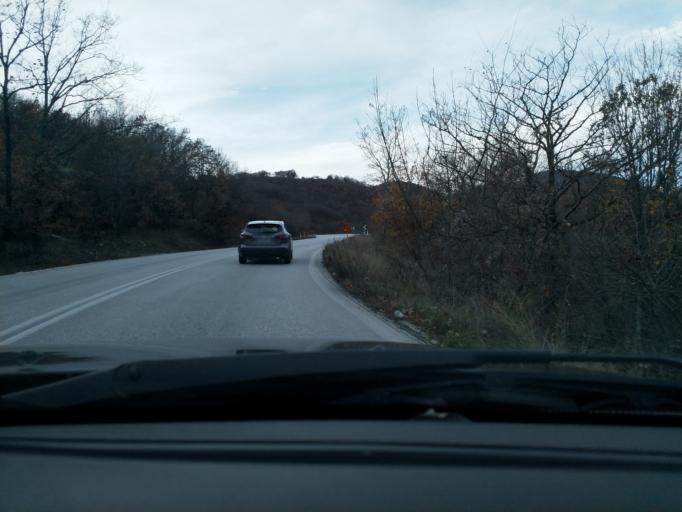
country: GR
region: Thessaly
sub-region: Trikala
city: Kastraki
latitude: 39.7413
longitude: 21.5264
